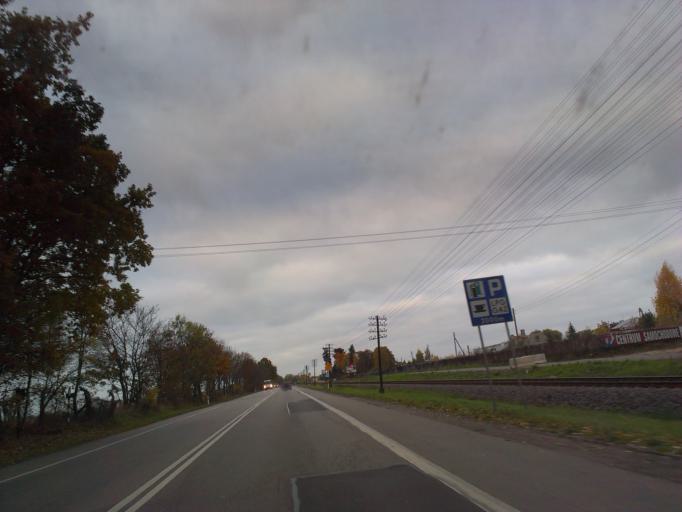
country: PL
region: Kujawsko-Pomorskie
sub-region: Powiat torunski
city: Lysomice
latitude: 53.0725
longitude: 18.6179
